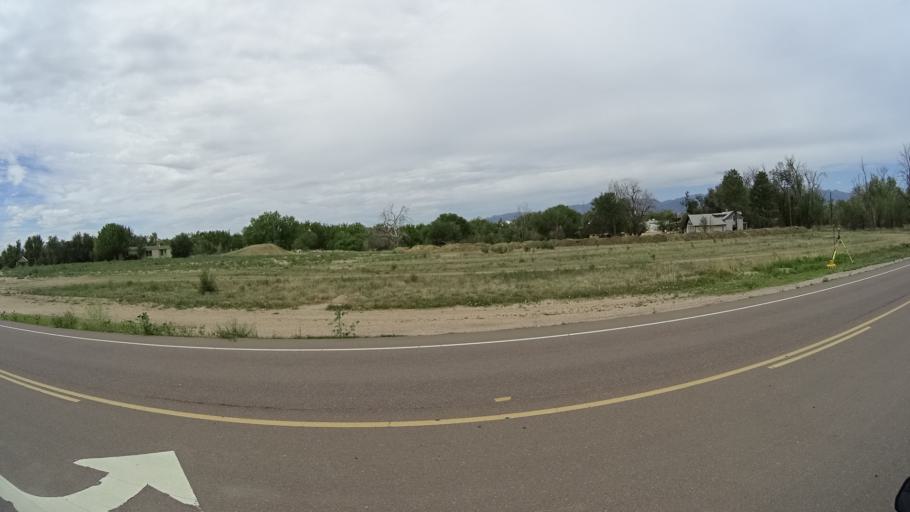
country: US
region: Colorado
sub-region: El Paso County
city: Fountain
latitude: 38.6712
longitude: -104.6953
